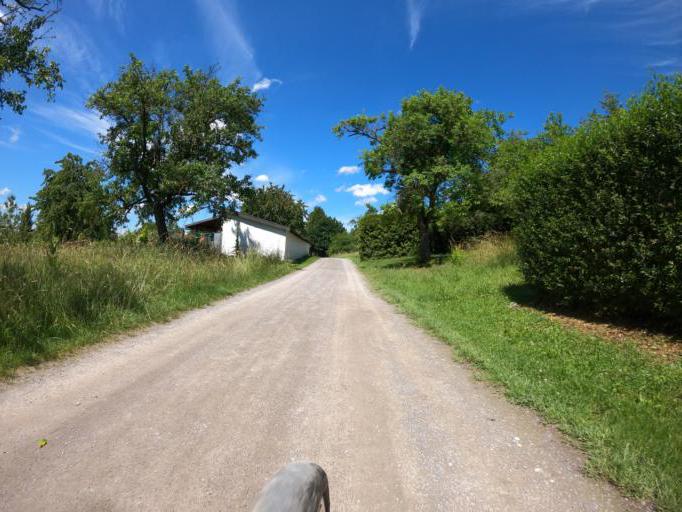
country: DE
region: Baden-Wuerttemberg
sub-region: Regierungsbezirk Stuttgart
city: Tamm
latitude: 48.9067
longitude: 9.1182
